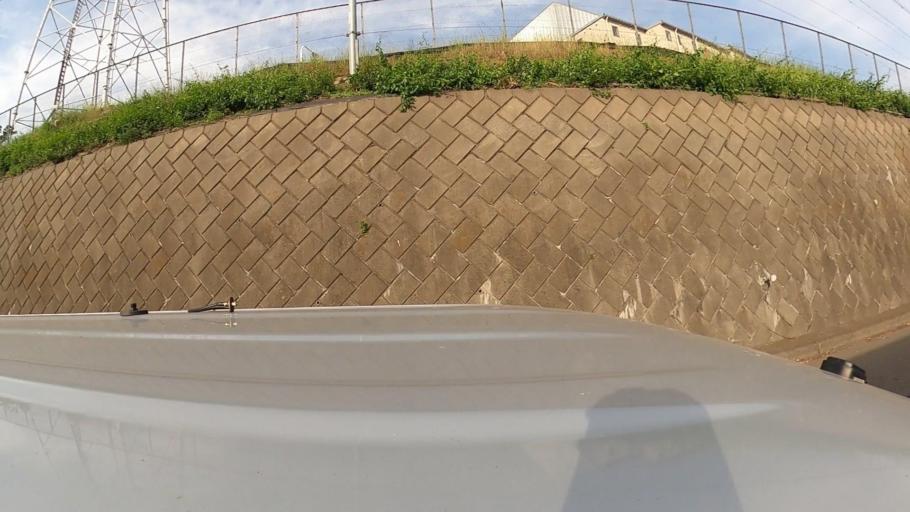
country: JP
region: Saitama
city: Oi
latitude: 35.8352
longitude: 139.5057
